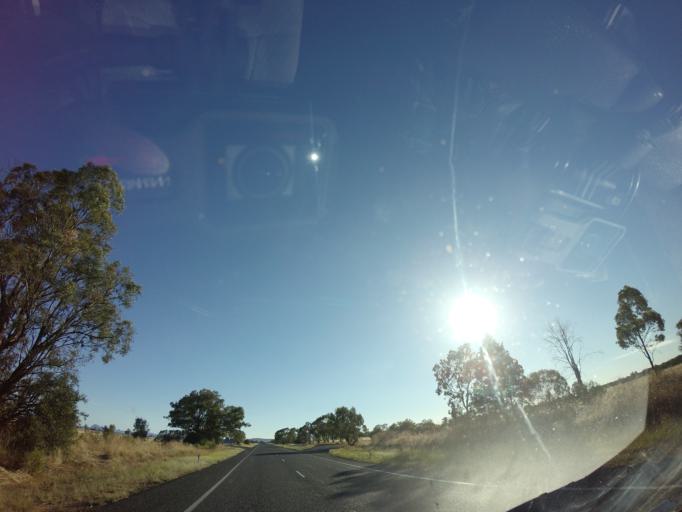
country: AU
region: New South Wales
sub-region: Gilgandra
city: Gilgandra
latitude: -31.5645
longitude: 148.7933
